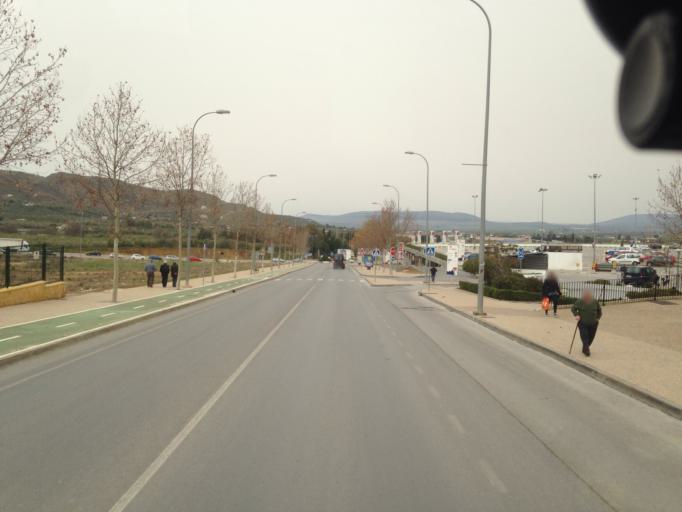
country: ES
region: Andalusia
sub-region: Provincia de Malaga
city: Antequera
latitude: 37.0246
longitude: -4.5720
